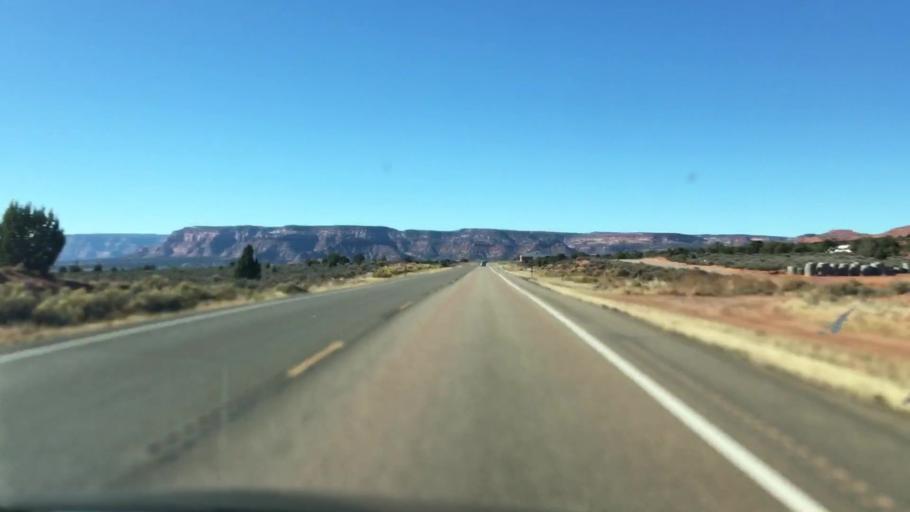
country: US
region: Utah
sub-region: Kane County
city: Kanab
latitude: 37.0269
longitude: -112.4722
